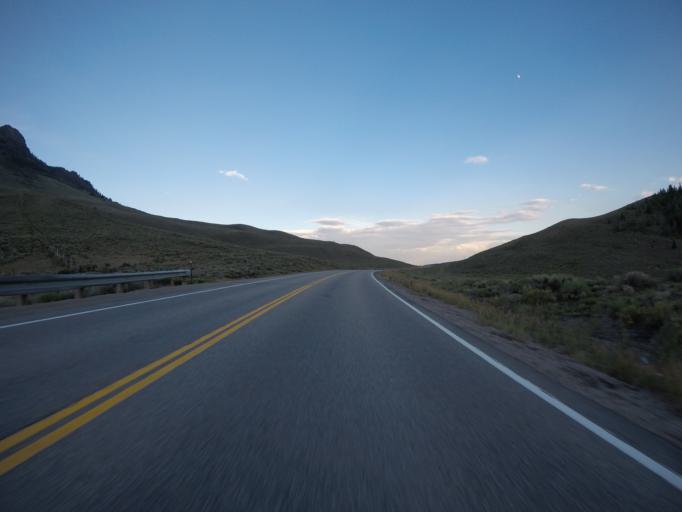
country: US
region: Colorado
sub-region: Grand County
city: Kremmling
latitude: 40.3108
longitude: -106.5115
